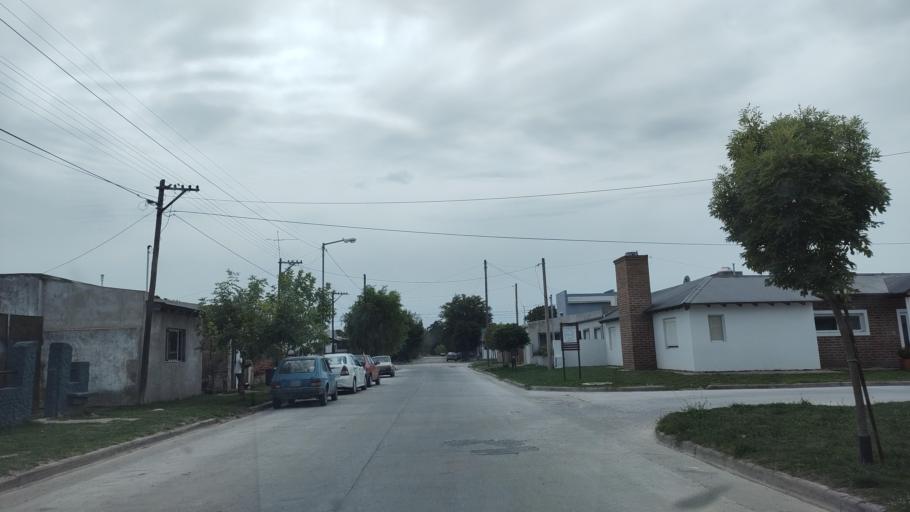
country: AR
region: Buenos Aires
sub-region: Partido de Loberia
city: Loberia
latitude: -38.1617
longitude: -58.7734
